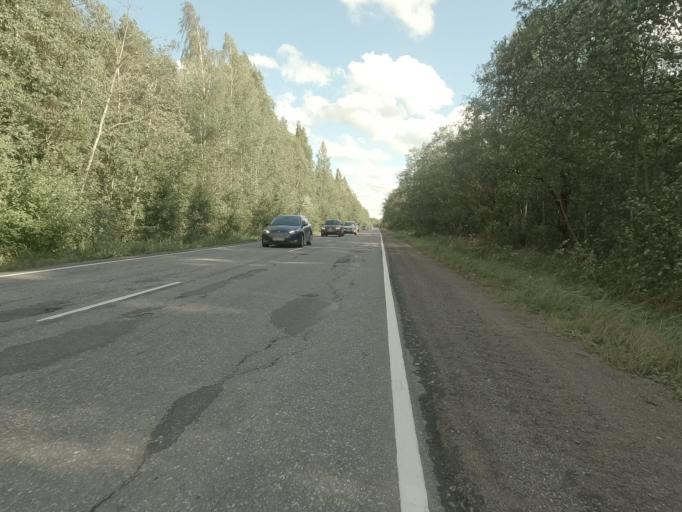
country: RU
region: Leningrad
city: Shcheglovo
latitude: 59.9939
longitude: 30.8795
